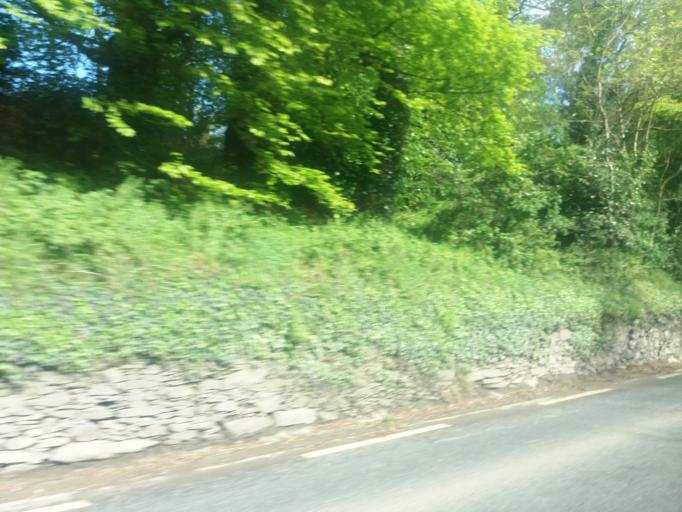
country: IE
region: Leinster
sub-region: Loch Garman
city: Enniscorthy
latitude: 52.5076
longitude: -6.5688
